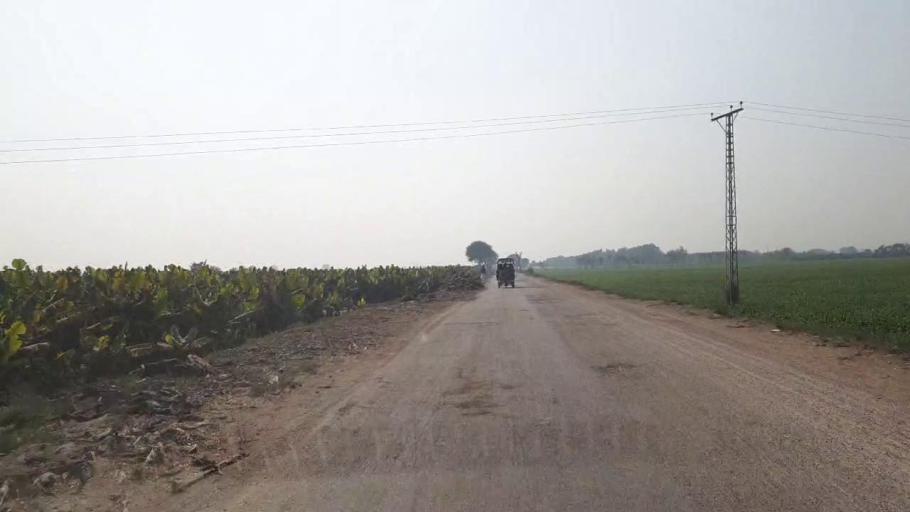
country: PK
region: Sindh
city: Hala
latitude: 25.8586
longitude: 68.4235
